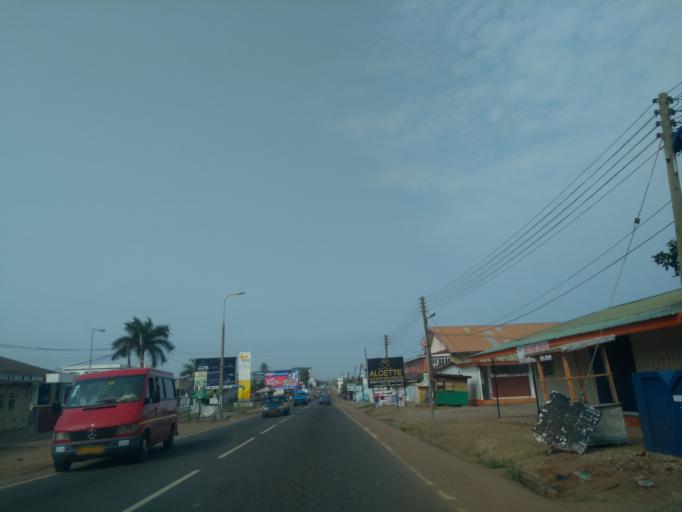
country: GH
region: Greater Accra
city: Accra
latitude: 5.5527
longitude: -0.1772
